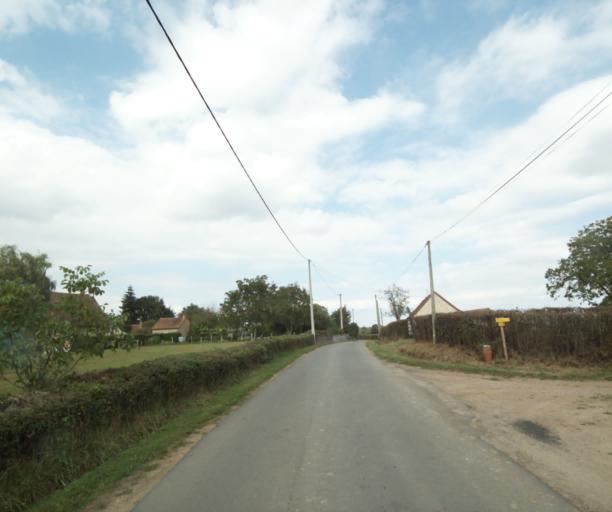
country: FR
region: Bourgogne
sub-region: Departement de Saone-et-Loire
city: Palinges
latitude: 46.4923
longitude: 4.1988
